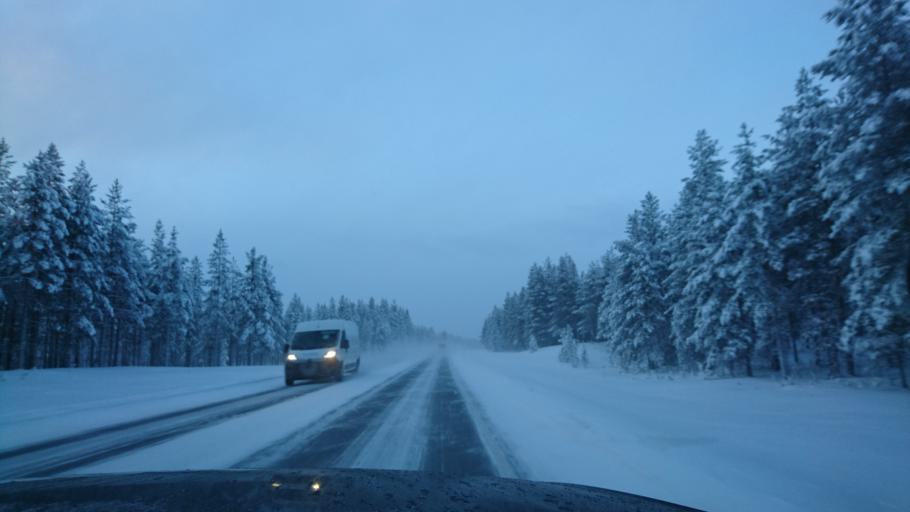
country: FI
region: Kainuu
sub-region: Kehys-Kainuu
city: Puolanka
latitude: 65.4326
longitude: 27.5752
